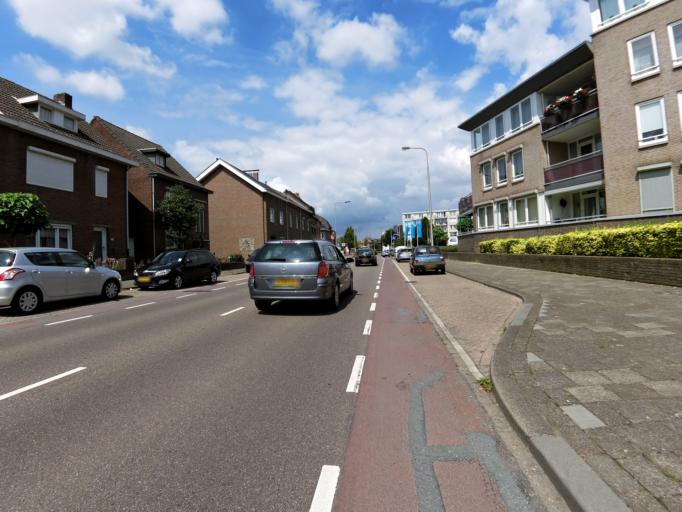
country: NL
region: Limburg
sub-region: Gemeente Kerkrade
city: Kerkrade
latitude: 50.8680
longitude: 6.0699
